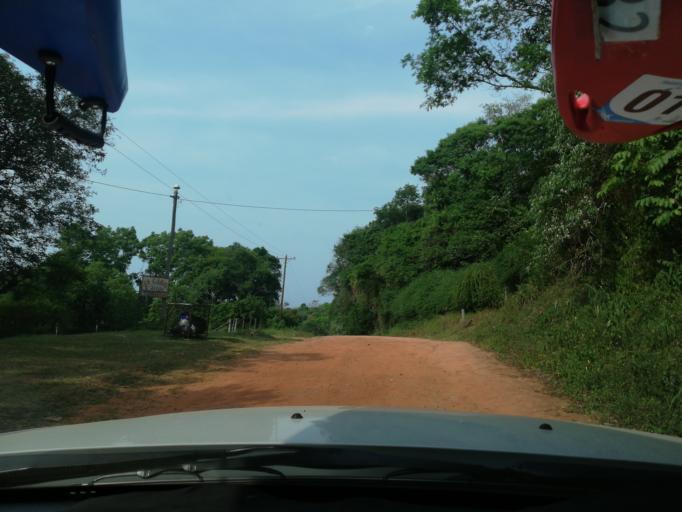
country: AR
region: Misiones
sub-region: Departamento de San Ignacio
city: San Ignacio
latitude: -27.2999
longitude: -55.5751
